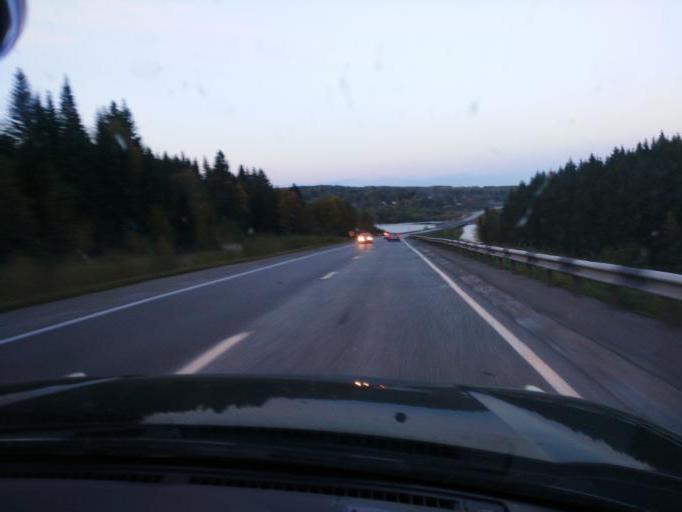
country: RU
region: Perm
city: Sylva
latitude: 58.2951
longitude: 56.8446
